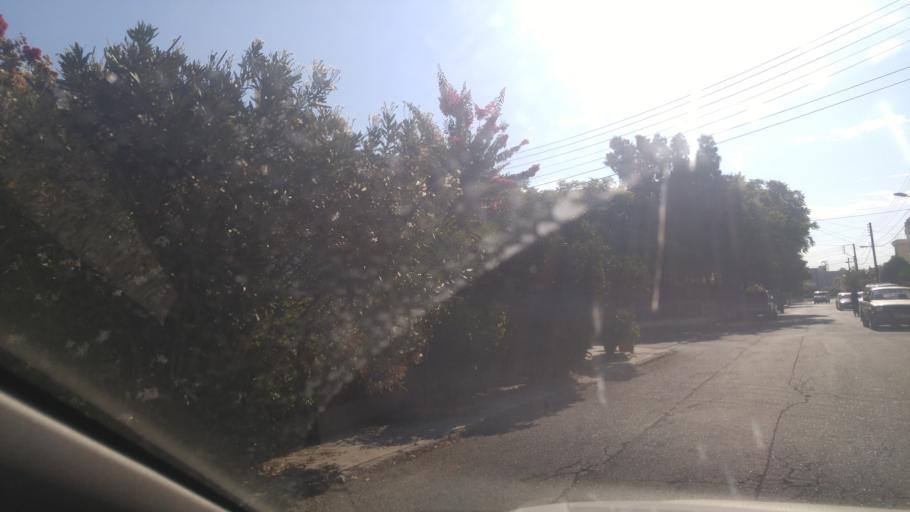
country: CY
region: Limassol
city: Limassol
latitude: 34.6955
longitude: 33.0478
